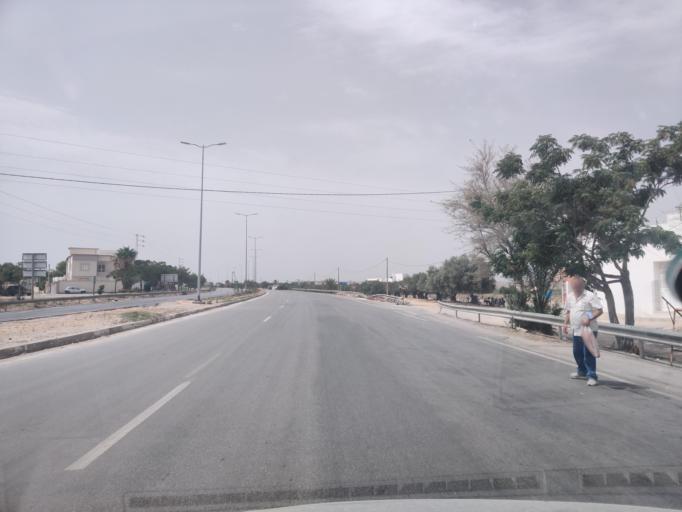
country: TN
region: Susah
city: Akouda
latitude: 35.8360
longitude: 10.5577
